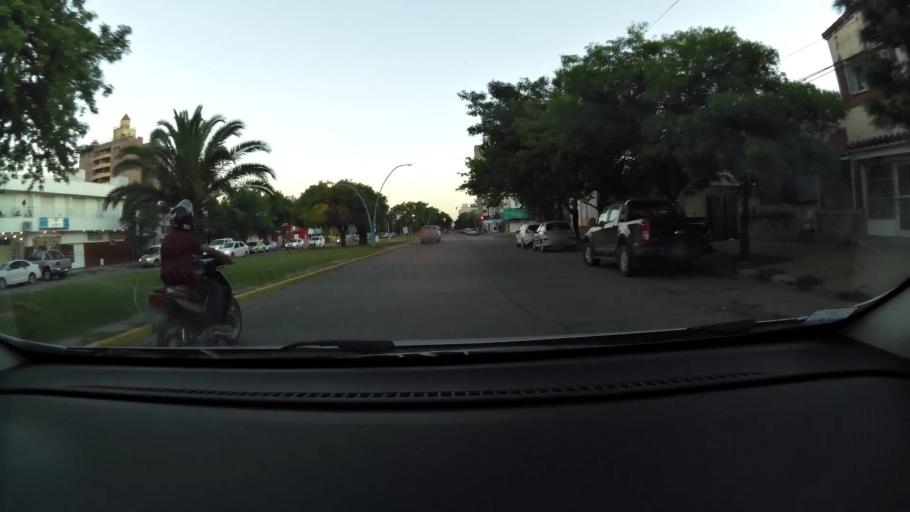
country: AR
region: Cordoba
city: Villa Maria
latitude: -32.4124
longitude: -63.2539
